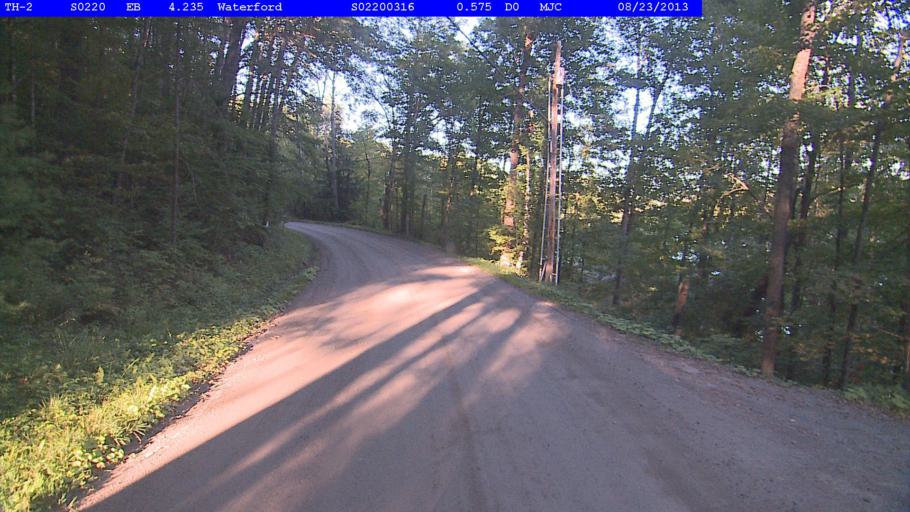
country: US
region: Vermont
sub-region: Caledonia County
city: Saint Johnsbury
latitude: 44.3393
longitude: -71.9855
